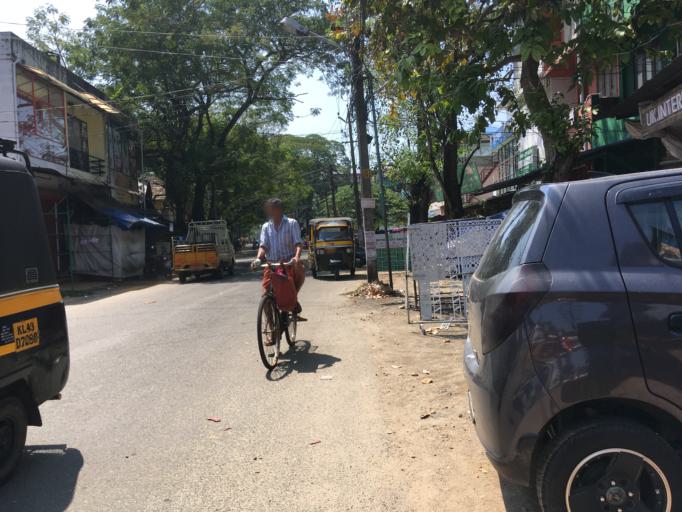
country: IN
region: Kerala
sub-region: Ernakulam
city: Cochin
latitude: 9.9602
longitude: 76.2456
